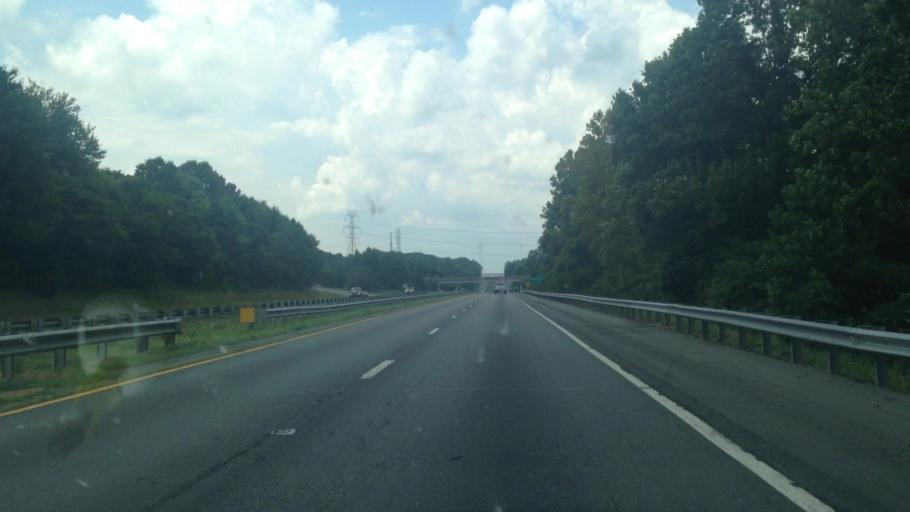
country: US
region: North Carolina
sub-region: Forsyth County
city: Tobaccoville
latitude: 36.2451
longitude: -80.3496
